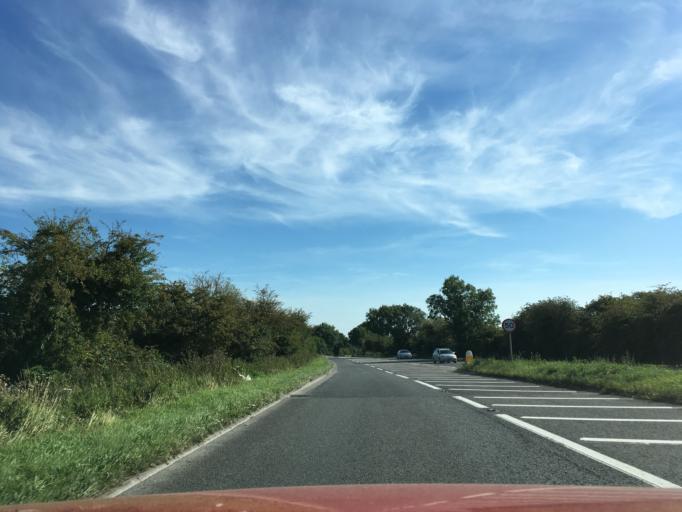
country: GB
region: England
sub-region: South Gloucestershire
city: Severn Beach
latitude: 51.5774
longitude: -2.6408
